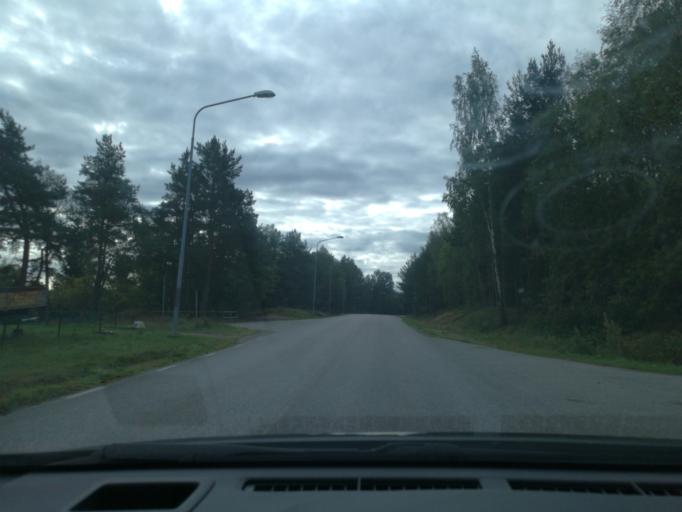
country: SE
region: Vaestmanland
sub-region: Kungsors Kommun
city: Kungsoer
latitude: 59.4123
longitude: 16.1067
